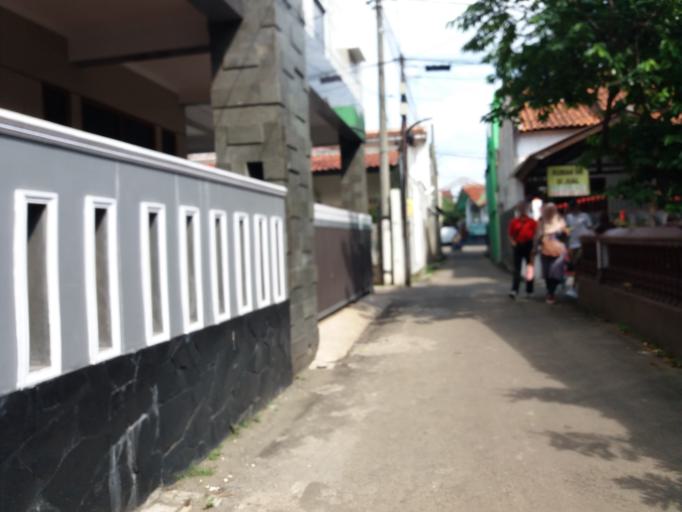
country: ID
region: West Java
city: Bandung
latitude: -6.9188
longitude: 107.6563
